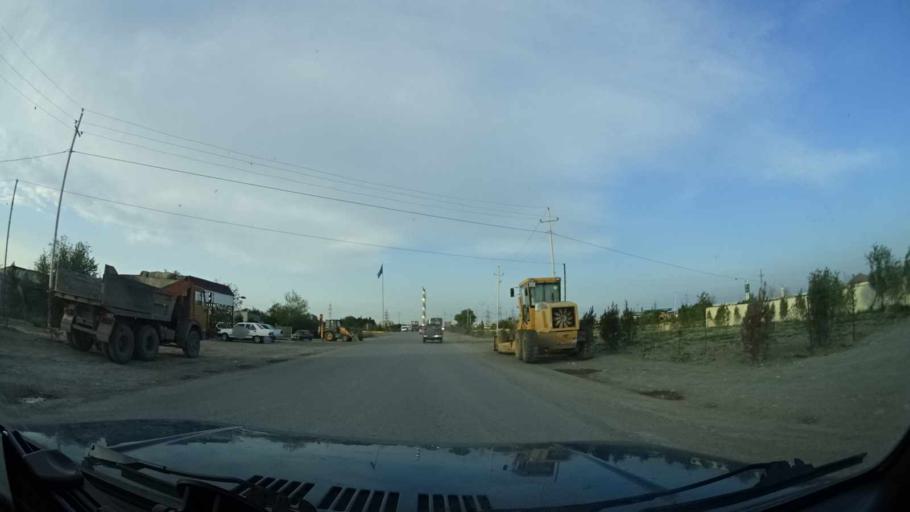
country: AZ
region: Abseron
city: Ceyranbatan
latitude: 40.5672
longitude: 49.6293
